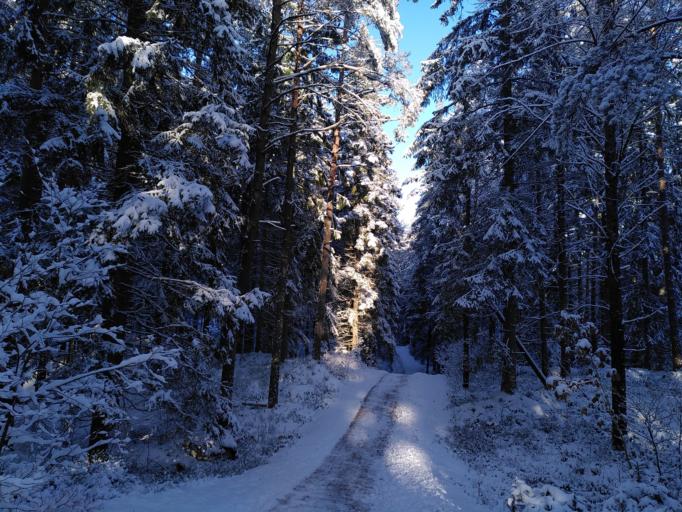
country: SE
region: Vaestra Goetaland
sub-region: Alingsas Kommun
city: Alingsas
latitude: 57.9243
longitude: 12.5766
